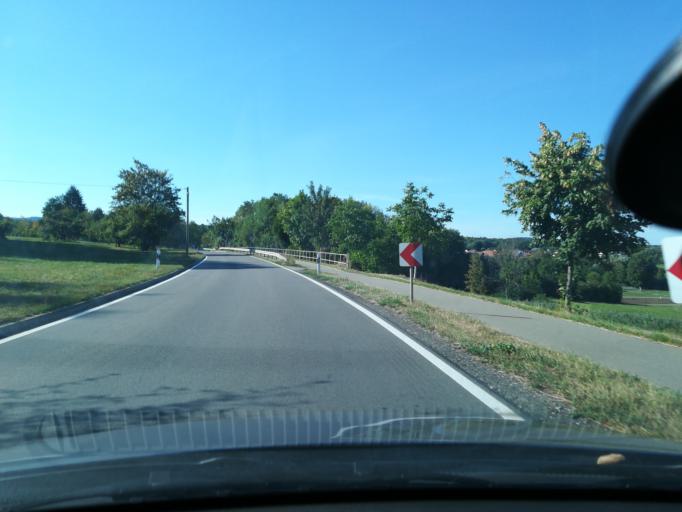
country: DE
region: Baden-Wuerttemberg
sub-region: Freiburg Region
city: Moos
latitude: 47.7318
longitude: 8.9005
